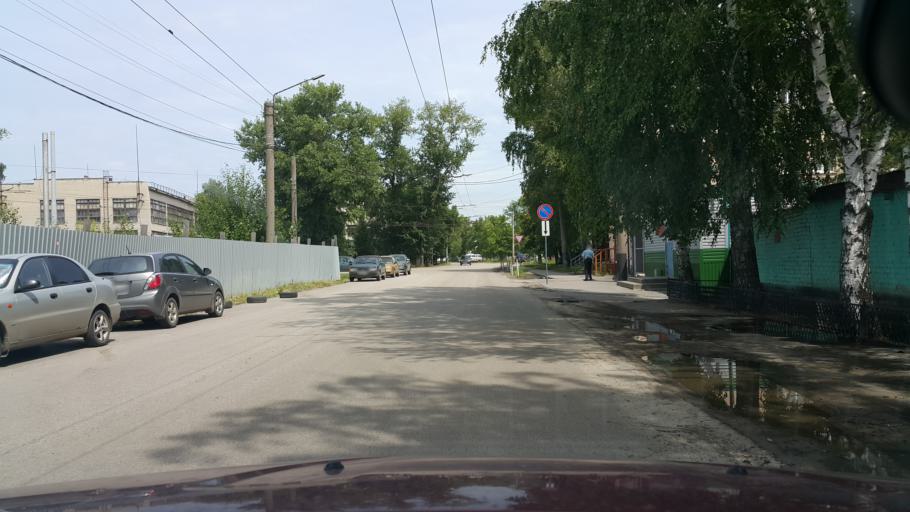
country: RU
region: Tambov
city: Donskoye
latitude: 52.7415
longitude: 41.4786
